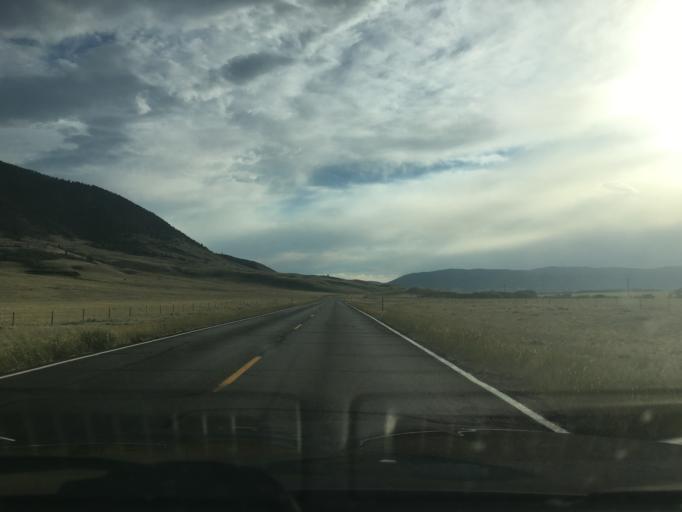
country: US
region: Wyoming
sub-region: Albany County
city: Laramie
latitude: 41.2896
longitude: -106.0332
